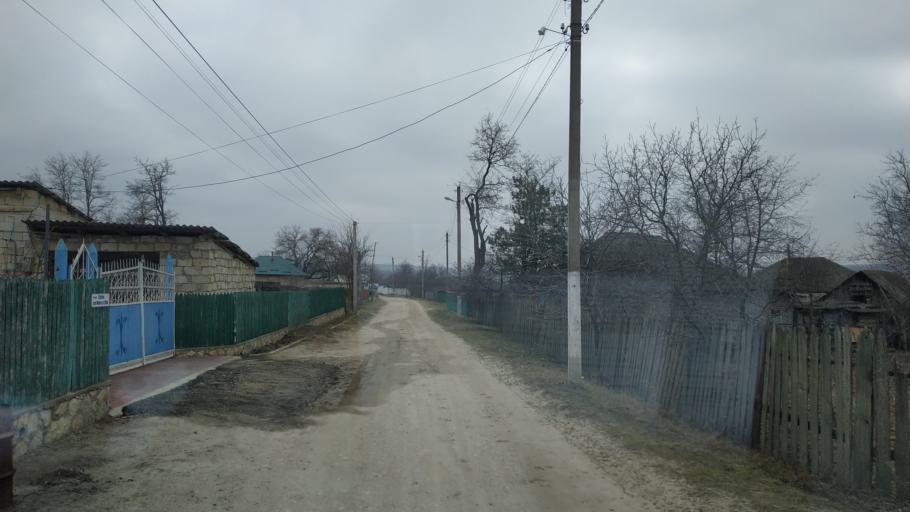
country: MD
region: Hincesti
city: Hincesti
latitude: 46.8881
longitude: 28.4049
